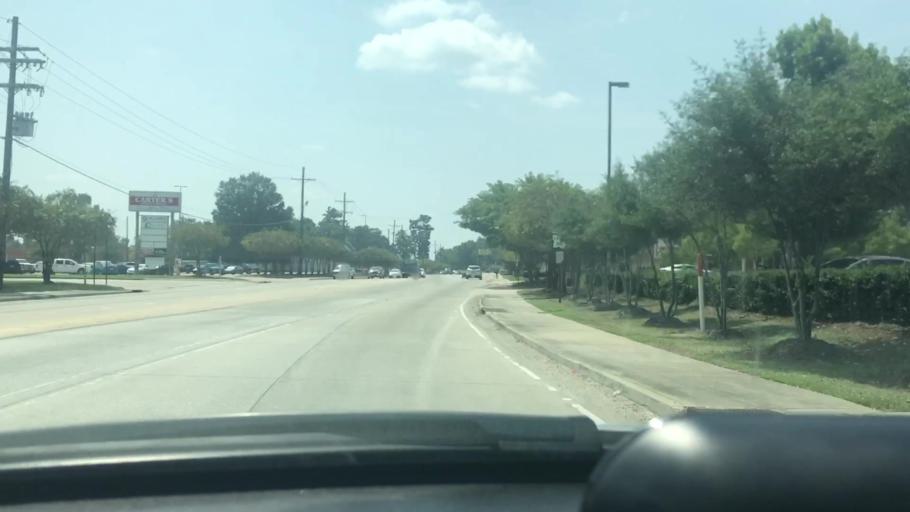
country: US
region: Louisiana
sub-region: Livingston Parish
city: Walker
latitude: 30.4875
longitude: -90.8618
